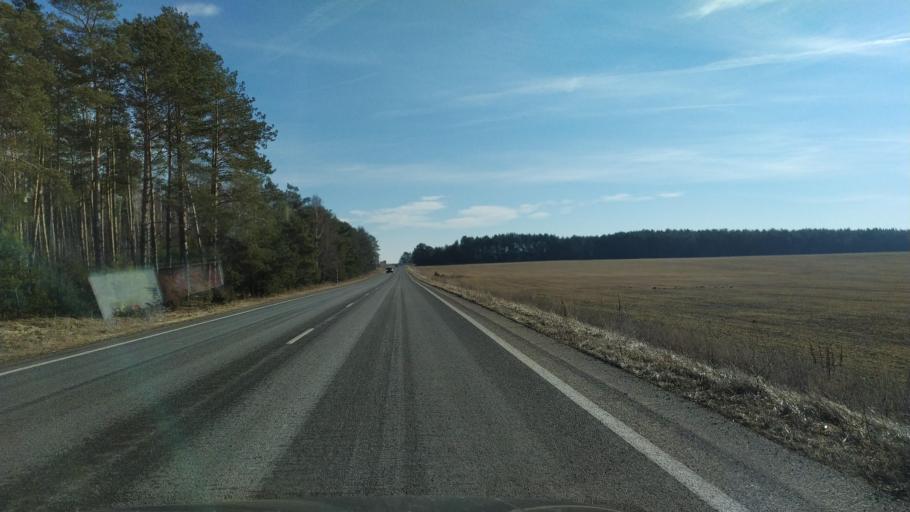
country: BY
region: Brest
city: Kamyanyets
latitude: 52.3968
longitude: 23.9165
